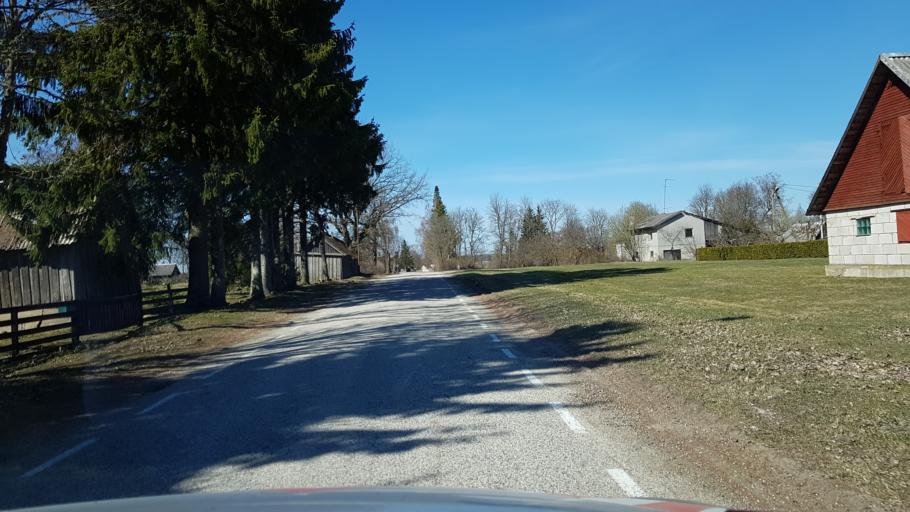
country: EE
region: Laeaene-Virumaa
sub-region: Vinni vald
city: Vinni
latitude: 59.0970
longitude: 26.5272
